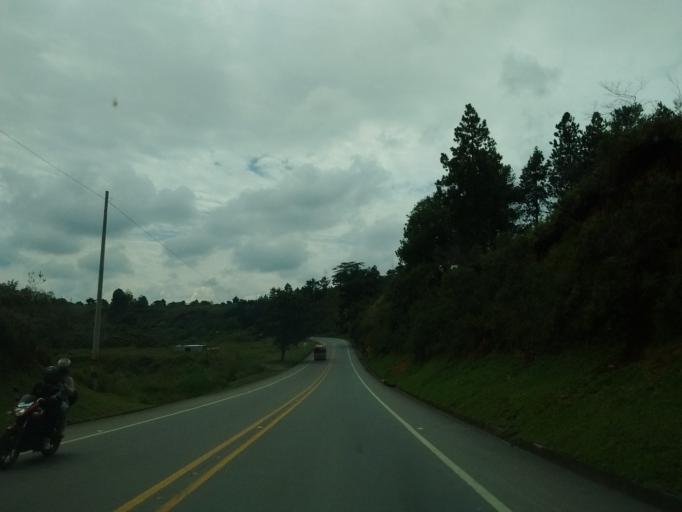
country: CO
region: Cauca
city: Cajibio
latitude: 2.5542
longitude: -76.5665
